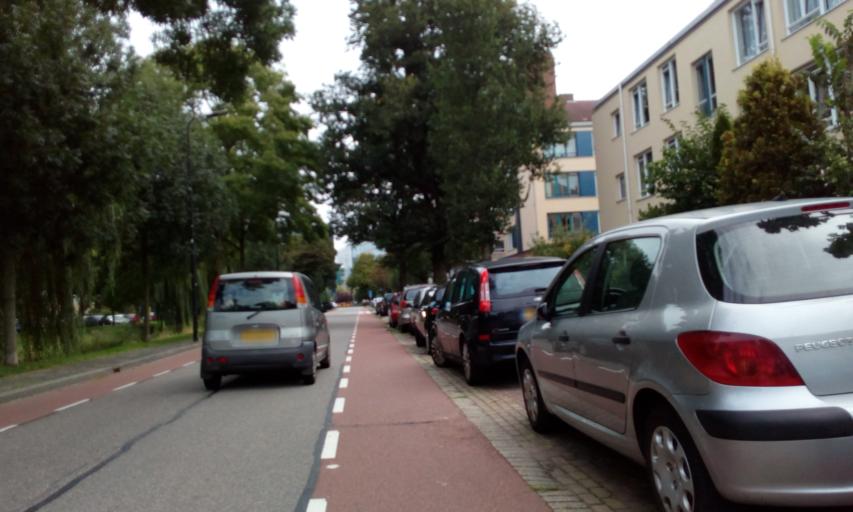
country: NL
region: South Holland
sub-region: Gemeente Rijswijk
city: Rijswijk
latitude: 52.0343
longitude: 4.3223
